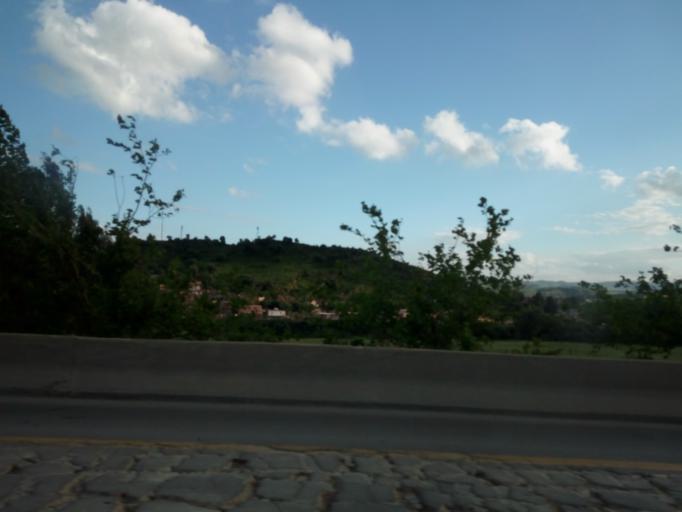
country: DZ
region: Tipaza
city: Hadjout
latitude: 36.3781
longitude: 2.4700
